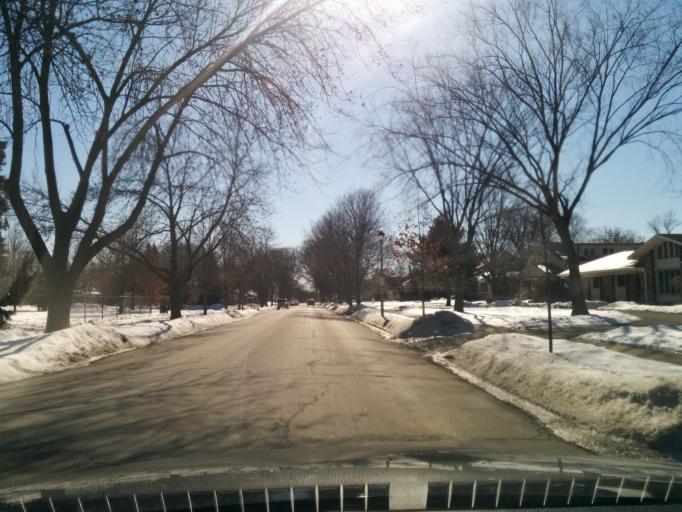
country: US
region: Illinois
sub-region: DuPage County
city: Elmhurst
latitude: 41.8877
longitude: -87.9303
